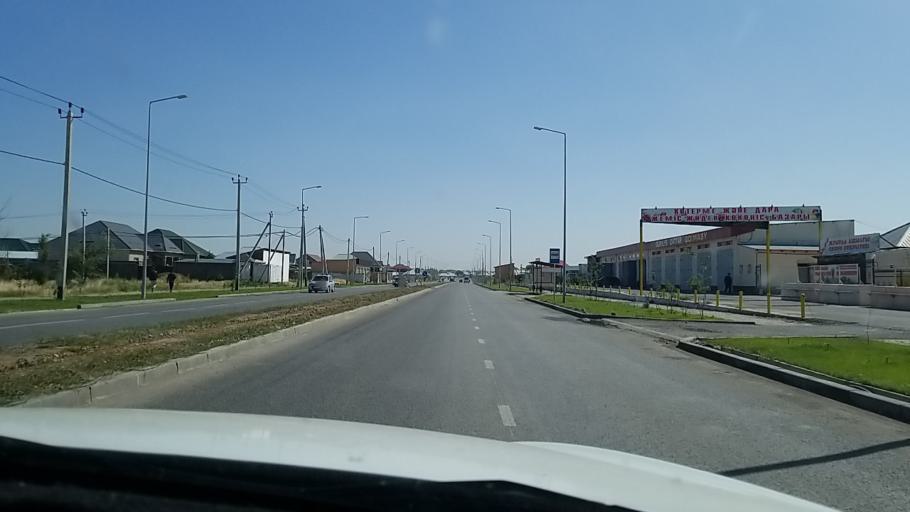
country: KZ
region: Ongtustik Qazaqstan
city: Shymkent
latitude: 42.3666
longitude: 69.5252
